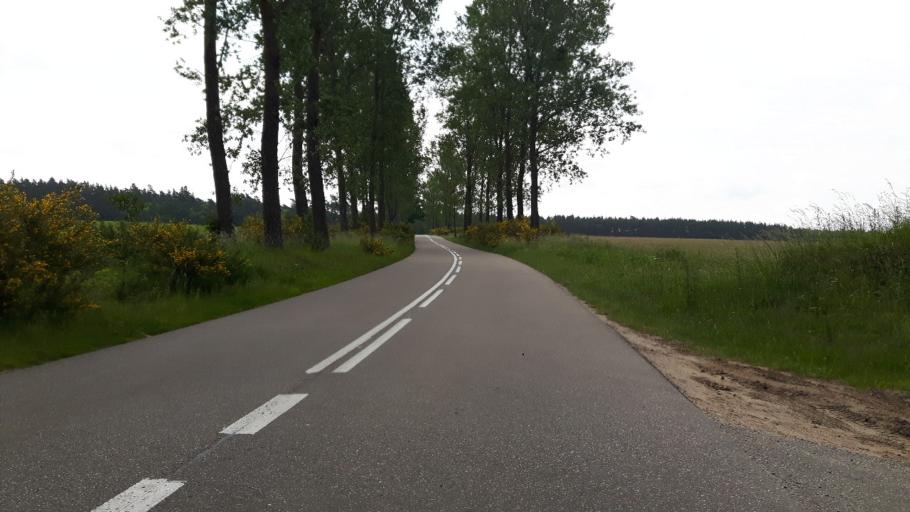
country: PL
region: Pomeranian Voivodeship
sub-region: Powiat leborski
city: Leba
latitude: 54.7487
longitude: 17.7114
